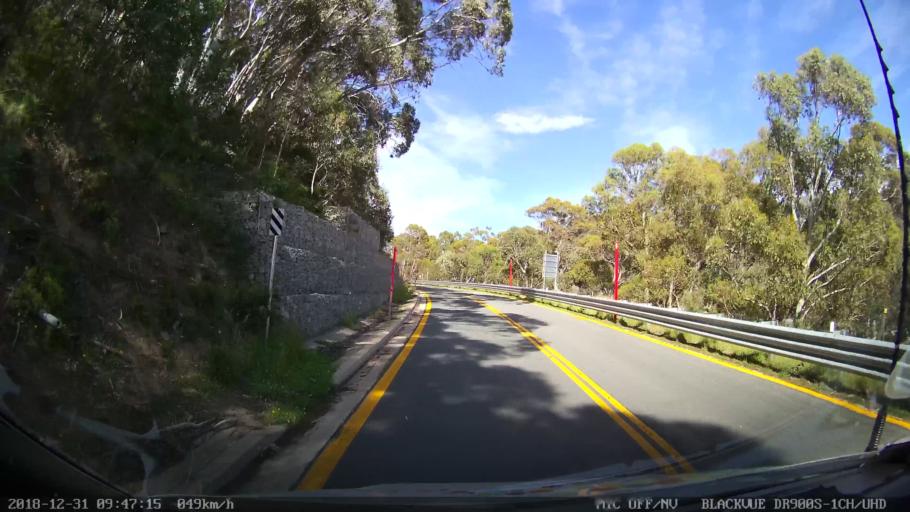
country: AU
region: New South Wales
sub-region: Snowy River
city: Jindabyne
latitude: -36.5077
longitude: 148.3032
